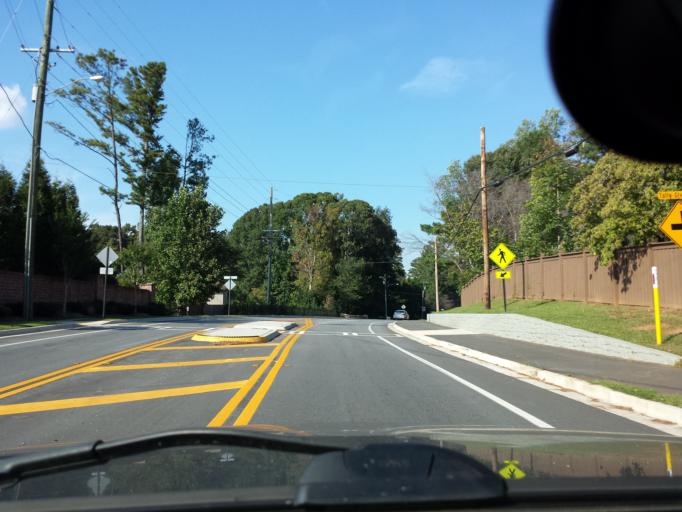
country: US
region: Georgia
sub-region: Fulton County
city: Roswell
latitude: 33.9797
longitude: -84.3912
